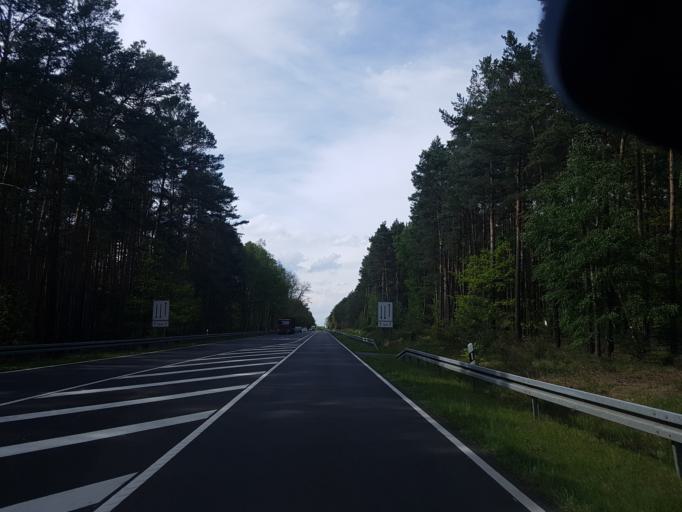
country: DE
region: Saxony
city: Gross Duben
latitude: 51.6601
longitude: 14.5293
